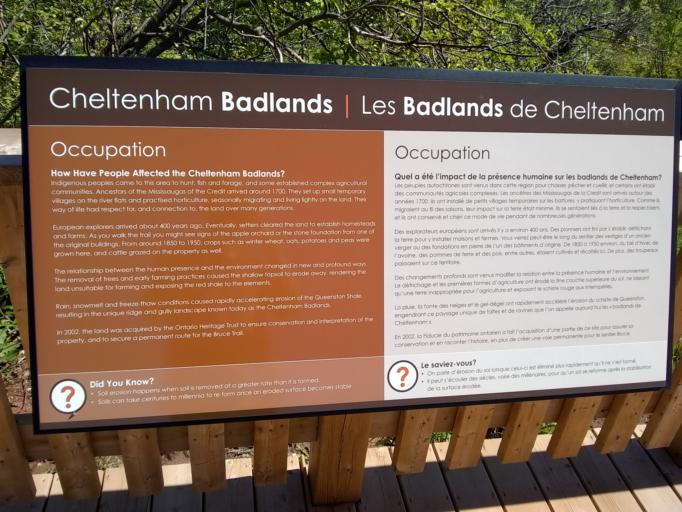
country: CA
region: Ontario
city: Brampton
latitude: 43.7740
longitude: -79.9443
